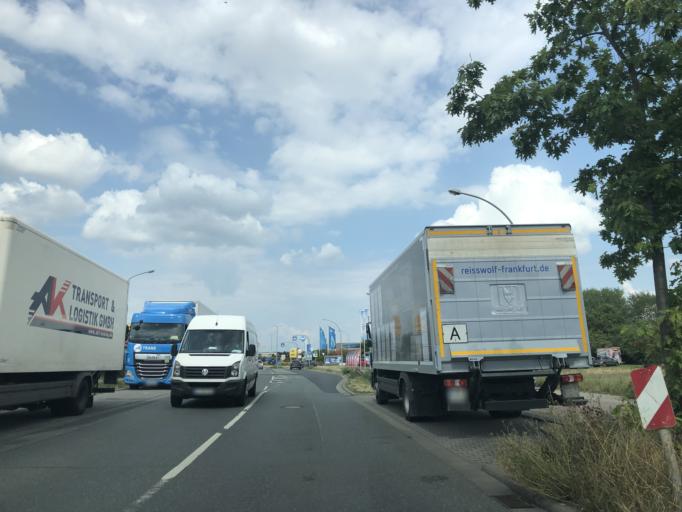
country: DE
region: Hesse
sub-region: Regierungsbezirk Darmstadt
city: Dietzenbach
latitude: 50.0121
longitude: 8.7931
